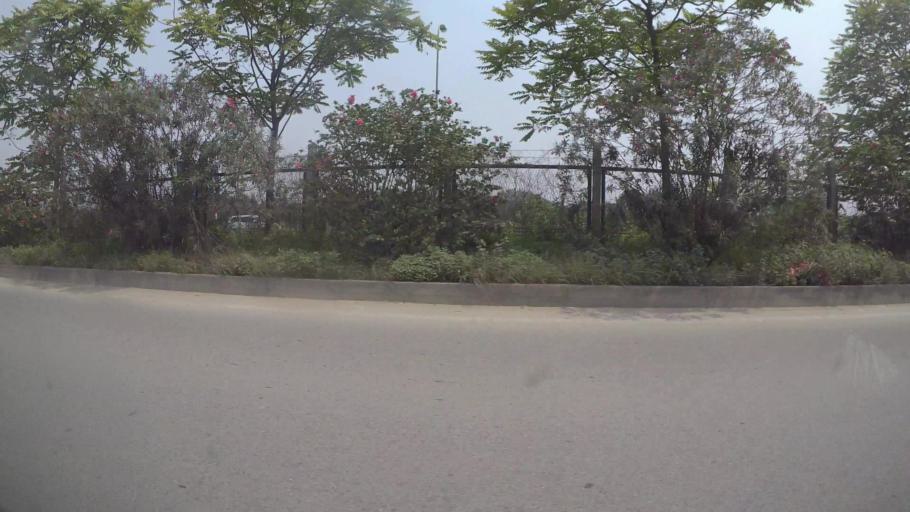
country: VN
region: Ha Noi
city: Cau Dien
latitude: 21.0068
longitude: 105.7584
